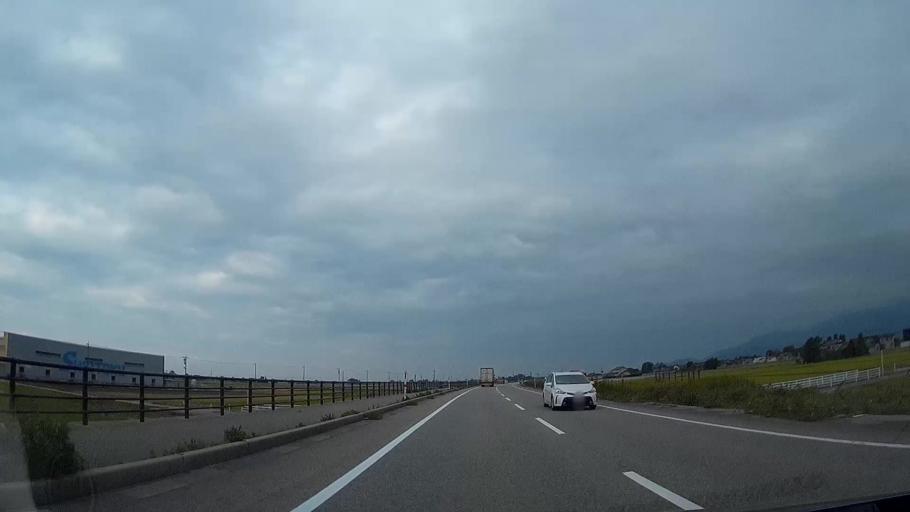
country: JP
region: Toyama
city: Nyuzen
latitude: 36.9244
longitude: 137.4705
